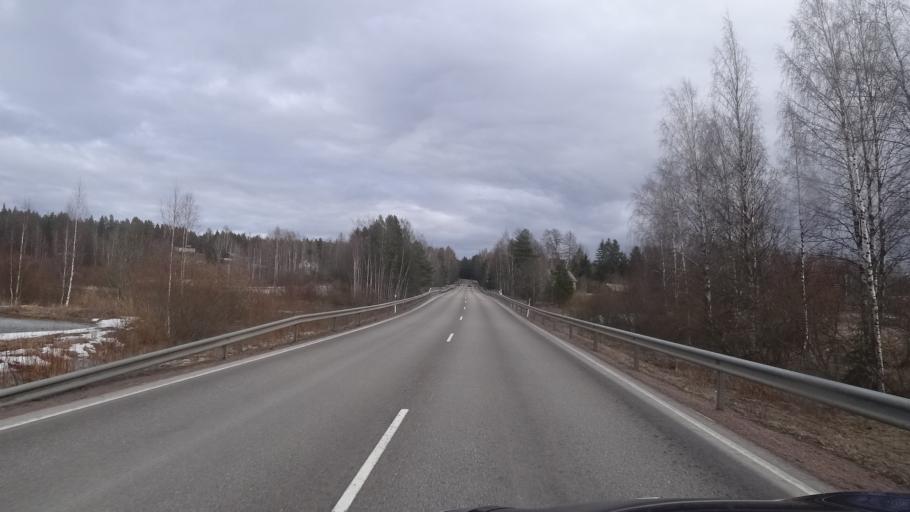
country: FI
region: Kymenlaakso
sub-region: Kouvola
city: Anjala
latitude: 60.6885
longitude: 26.7440
